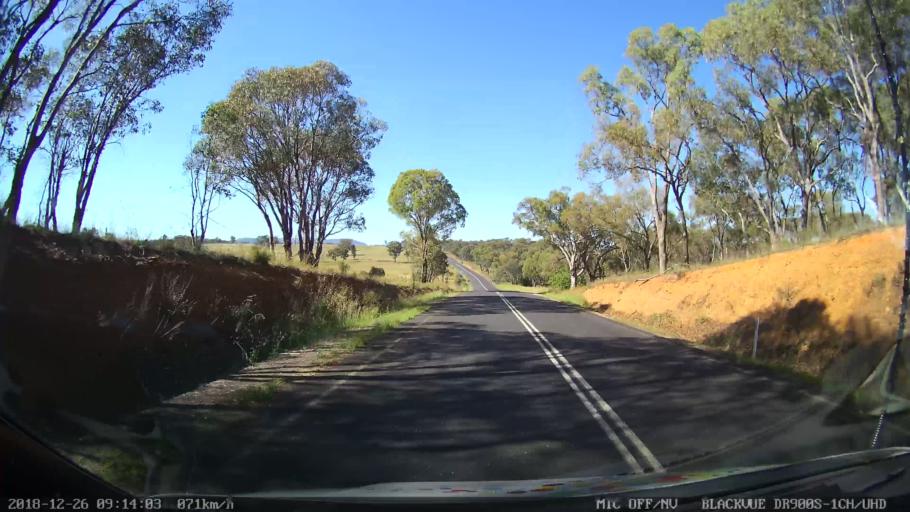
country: AU
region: New South Wales
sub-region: Mid-Western Regional
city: Kandos
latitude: -32.7742
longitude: 149.9797
